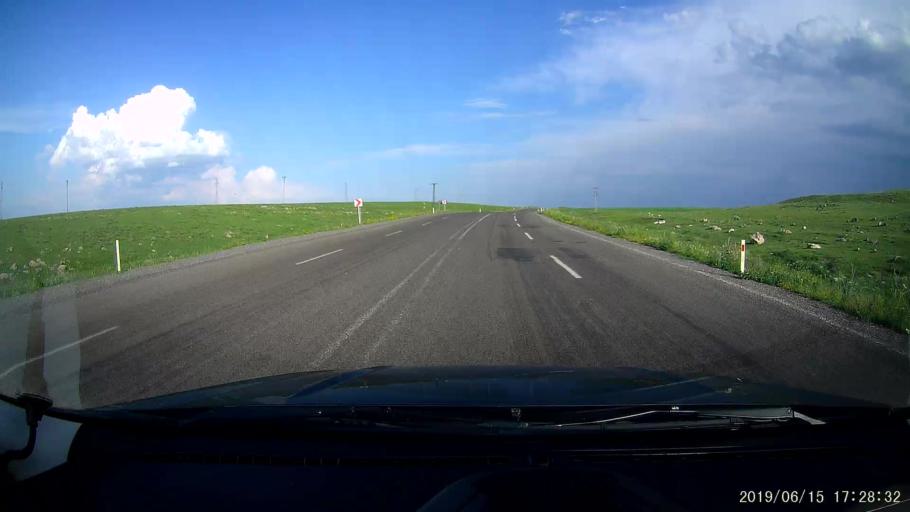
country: TR
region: Kars
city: Basgedikler
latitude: 40.5959
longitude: 43.4441
